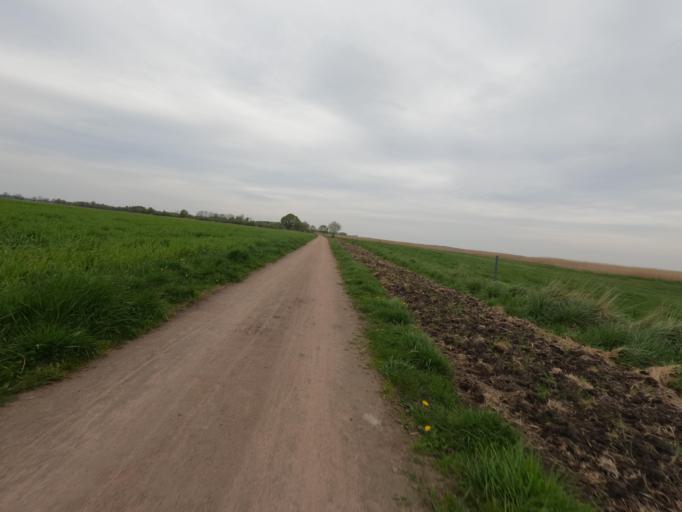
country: DE
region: Mecklenburg-Vorpommern
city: Ostseebad Dierhagen
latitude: 54.2821
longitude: 12.3747
